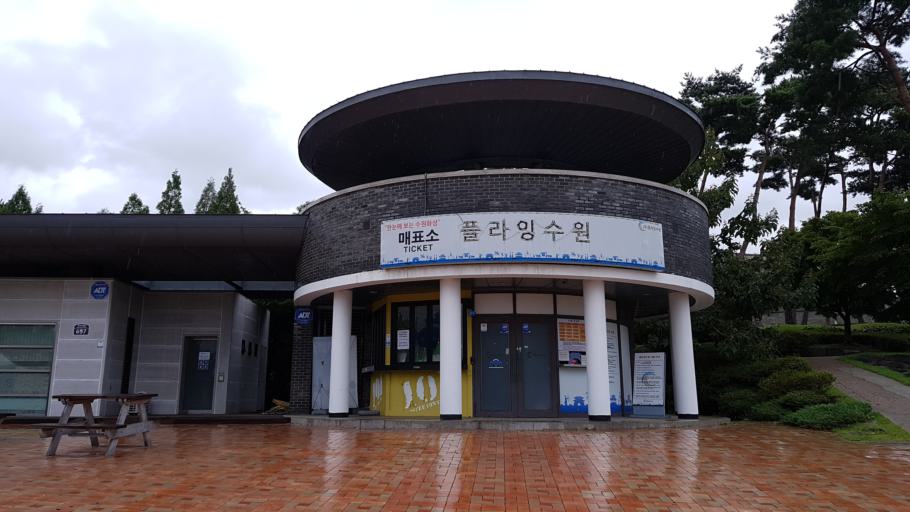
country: KR
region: Gyeonggi-do
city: Suwon-si
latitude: 37.2873
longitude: 127.0260
